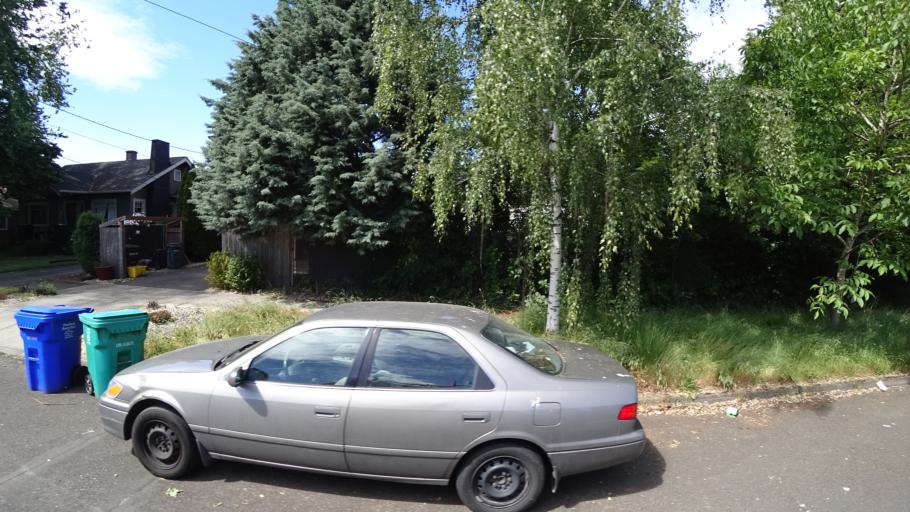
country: US
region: Washington
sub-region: Clark County
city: Vancouver
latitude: 45.5887
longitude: -122.7195
